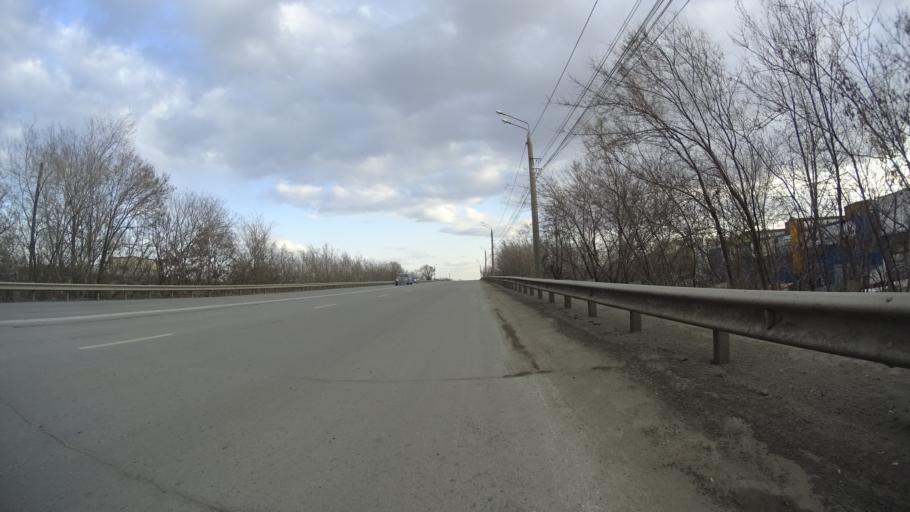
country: RU
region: Chelyabinsk
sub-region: Gorod Chelyabinsk
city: Chelyabinsk
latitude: 55.1042
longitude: 61.3873
